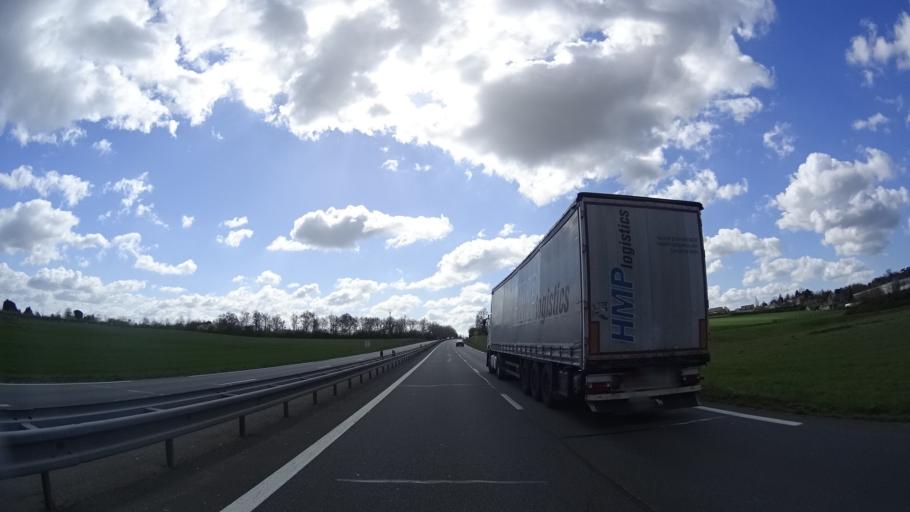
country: FR
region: Pays de la Loire
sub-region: Departement de Maine-et-Loire
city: Brissac-Quince
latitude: 47.3555
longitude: -0.4408
